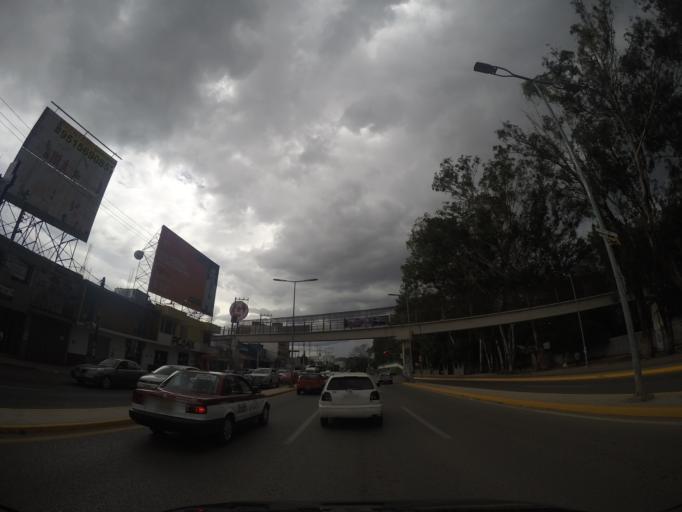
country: MX
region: Oaxaca
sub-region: Santa Cruz Amilpas
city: Santa Cruz Amilpas
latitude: 17.0690
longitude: -96.6966
